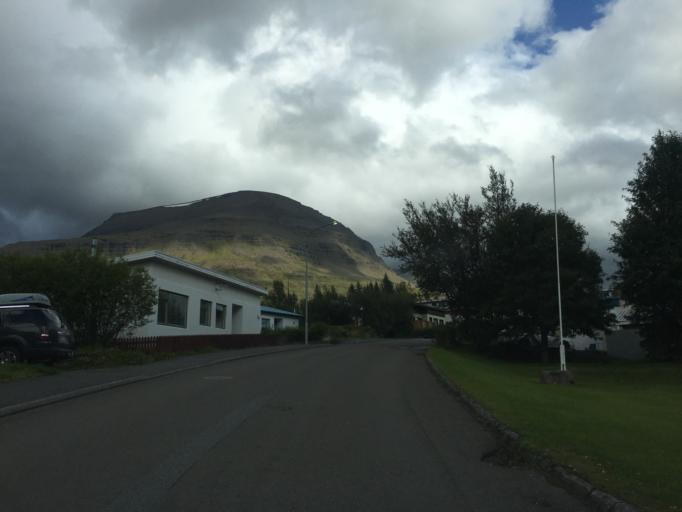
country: IS
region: East
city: Reydarfjoerdur
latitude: 65.0356
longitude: -14.2154
